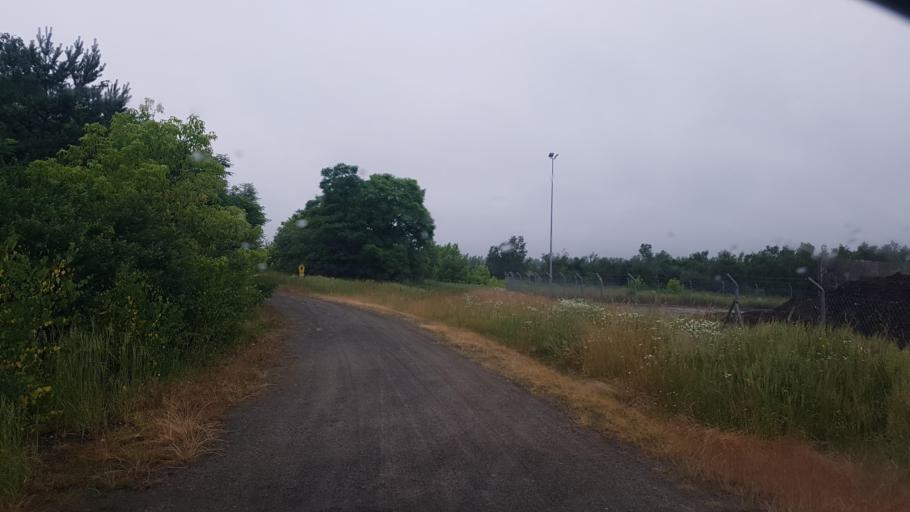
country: DE
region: Brandenburg
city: Lauchhammer
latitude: 51.5450
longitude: 13.7458
